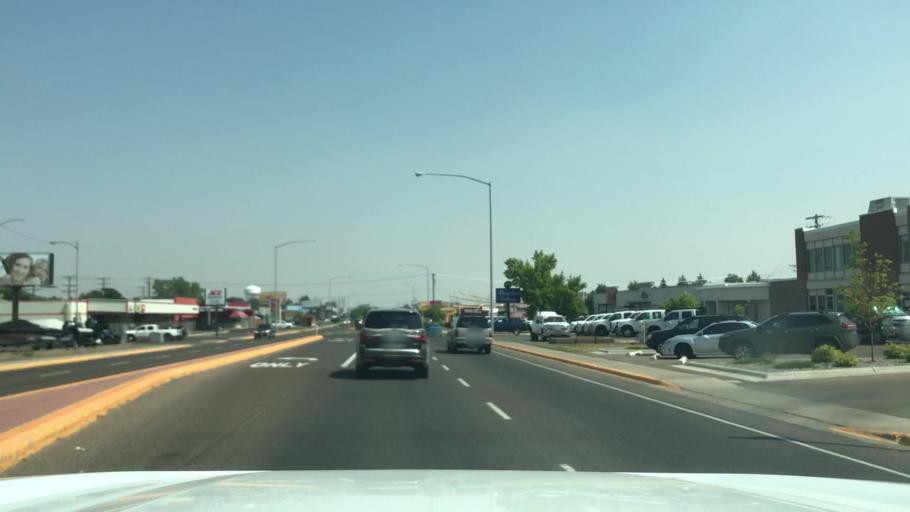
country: US
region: Montana
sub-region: Cascade County
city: Great Falls
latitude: 47.4940
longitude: -111.2476
